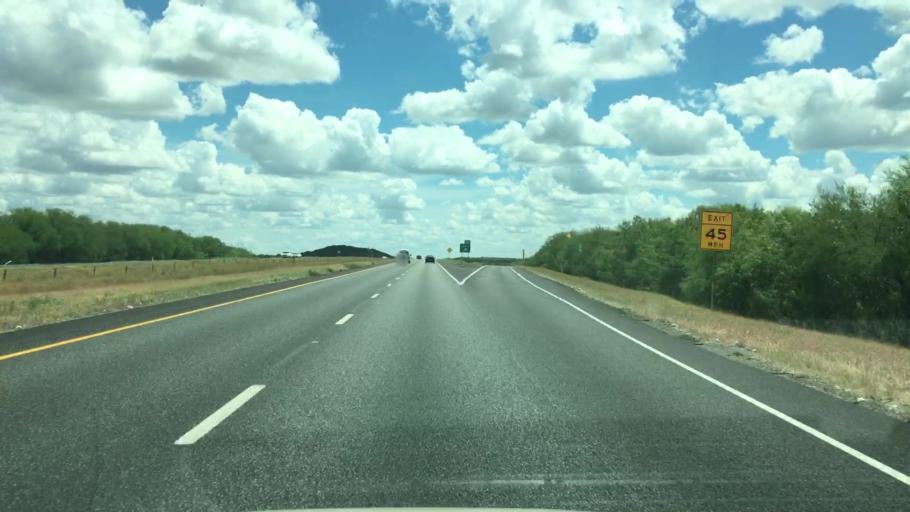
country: US
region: Texas
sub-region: Atascosa County
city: Pleasanton
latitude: 28.7382
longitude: -98.2910
